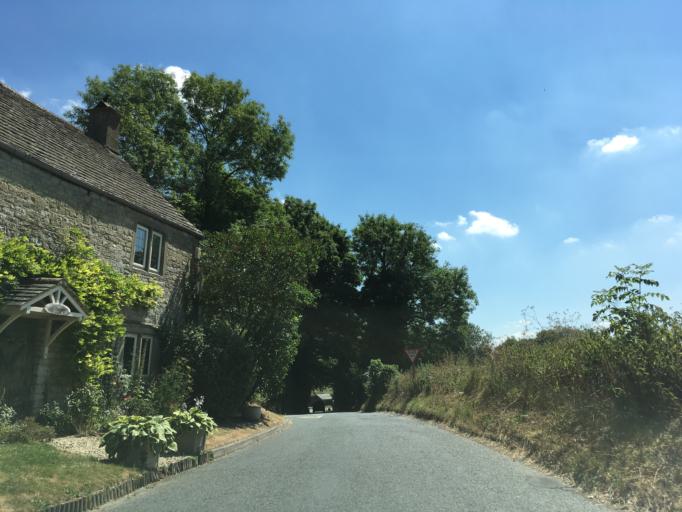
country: GB
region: England
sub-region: Gloucestershire
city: Chalford
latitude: 51.7487
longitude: -2.1390
